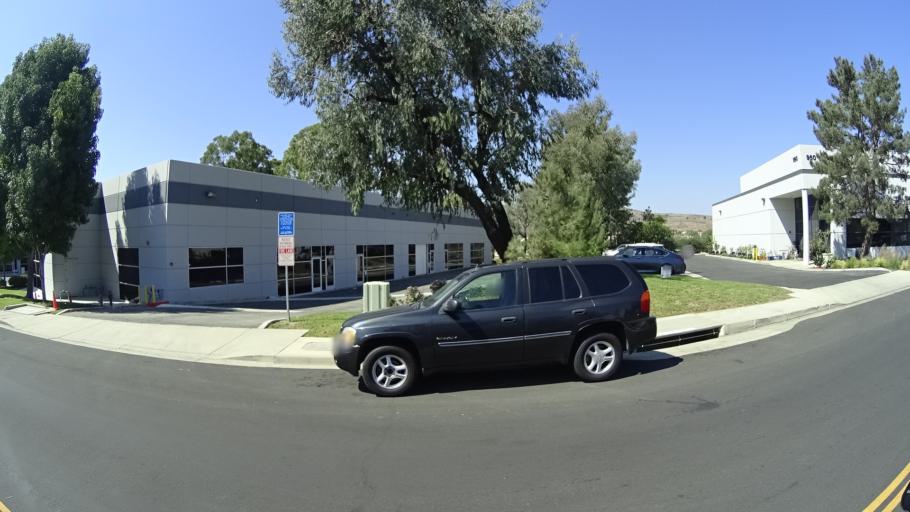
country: US
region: California
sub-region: Orange County
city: San Clemente
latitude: 33.4525
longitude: -117.6047
